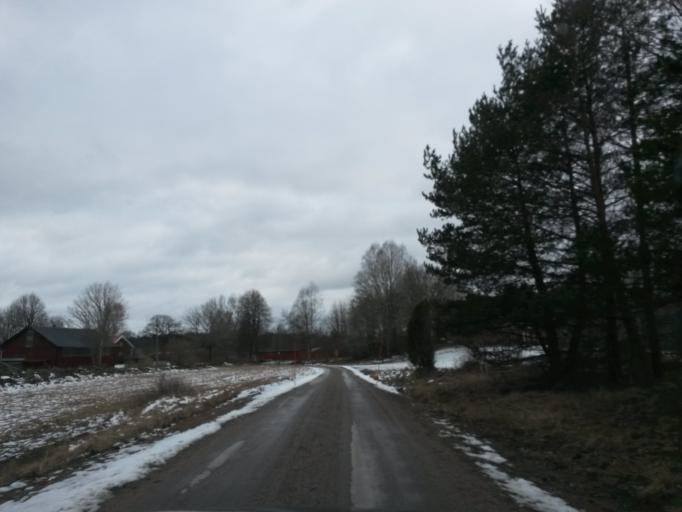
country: SE
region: Vaestra Goetaland
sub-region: Vargarda Kommun
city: Vargarda
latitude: 58.0341
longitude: 12.9022
